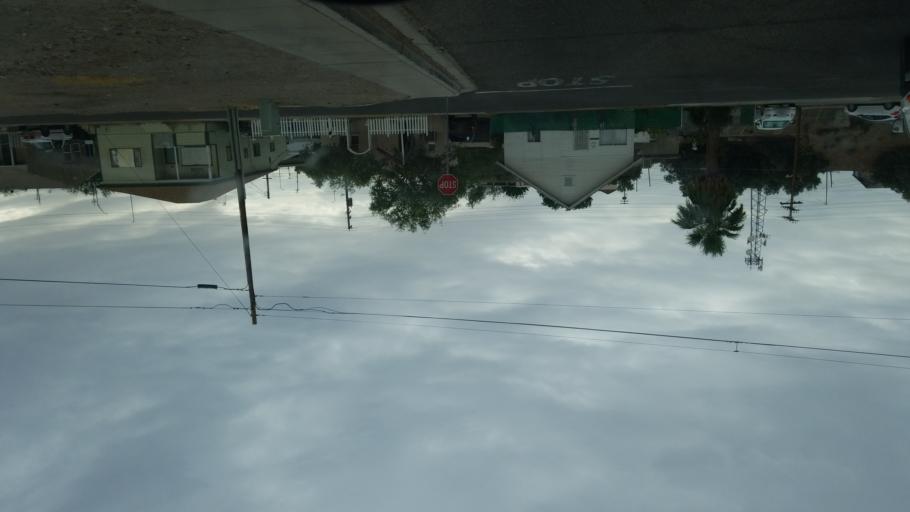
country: US
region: California
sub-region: San Bernardino County
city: Needles
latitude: 34.8431
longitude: -114.6106
